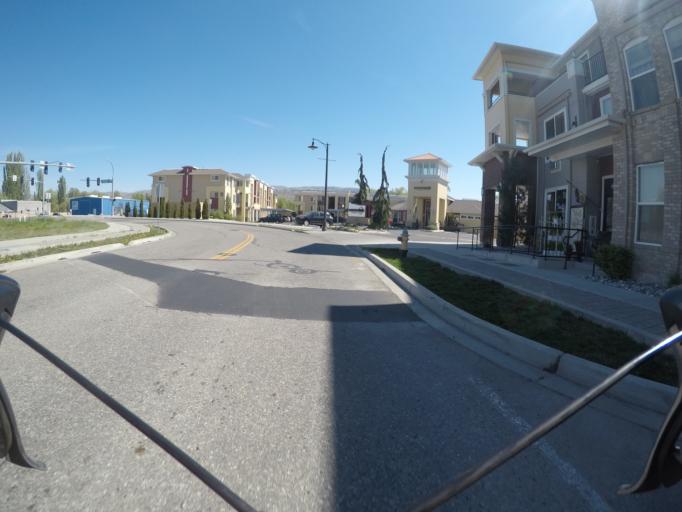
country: US
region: Washington
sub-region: Chelan County
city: Wenatchee
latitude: 47.4364
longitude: -120.3159
